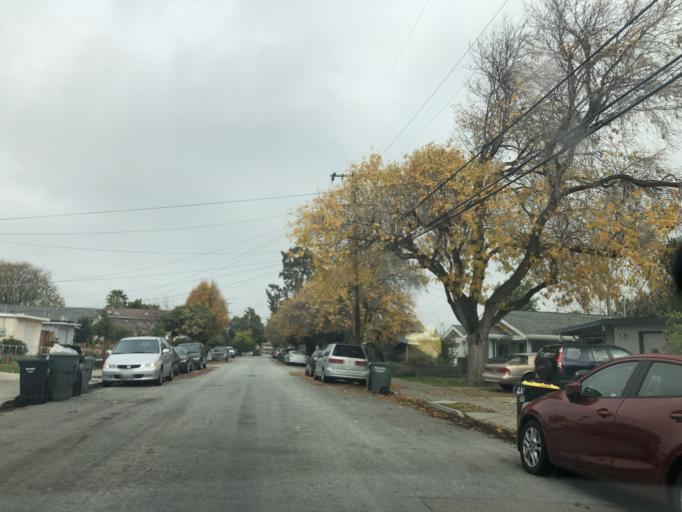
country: US
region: California
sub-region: Santa Clara County
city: Sunnyvale
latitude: 37.3888
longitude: -122.0130
